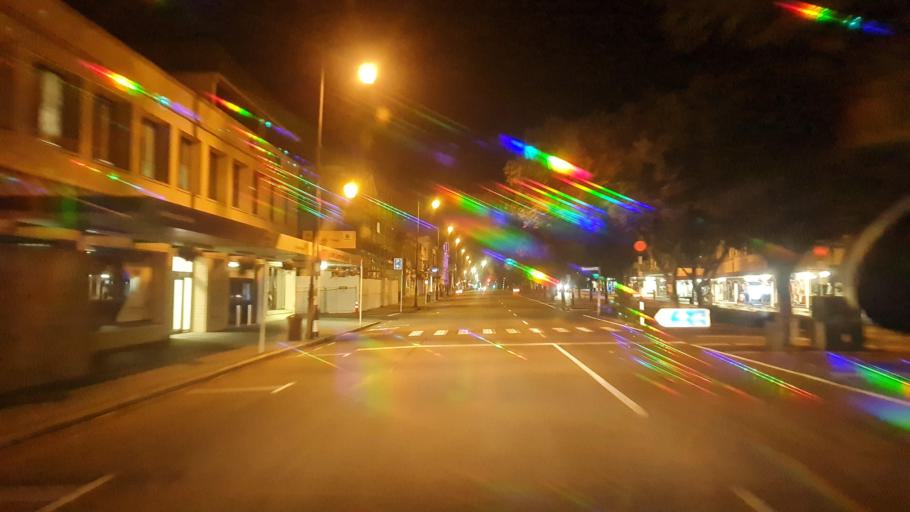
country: NZ
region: Otago
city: Oamaru
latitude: -45.1004
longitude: 170.9695
